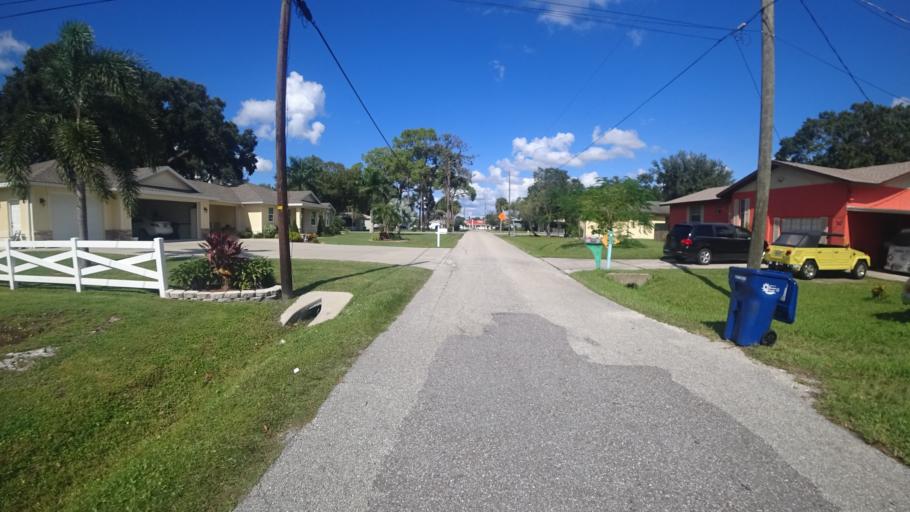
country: US
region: Florida
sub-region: Manatee County
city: Ellenton
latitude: 27.5201
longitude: -82.5302
